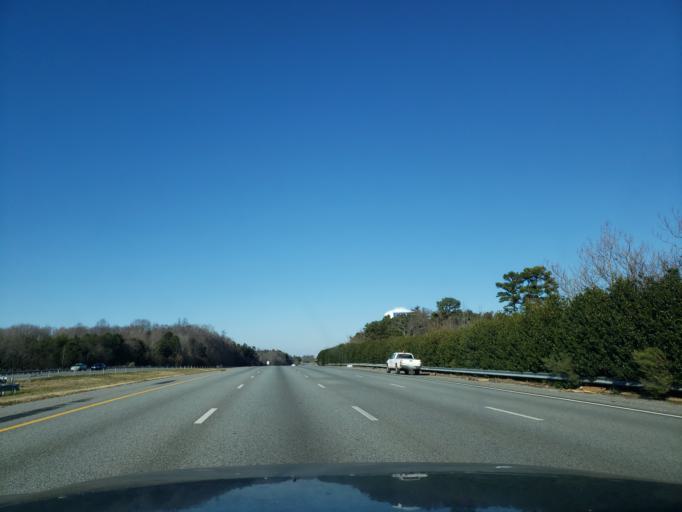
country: US
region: North Carolina
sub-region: Guilford County
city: High Point
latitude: 35.9672
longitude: -79.9747
